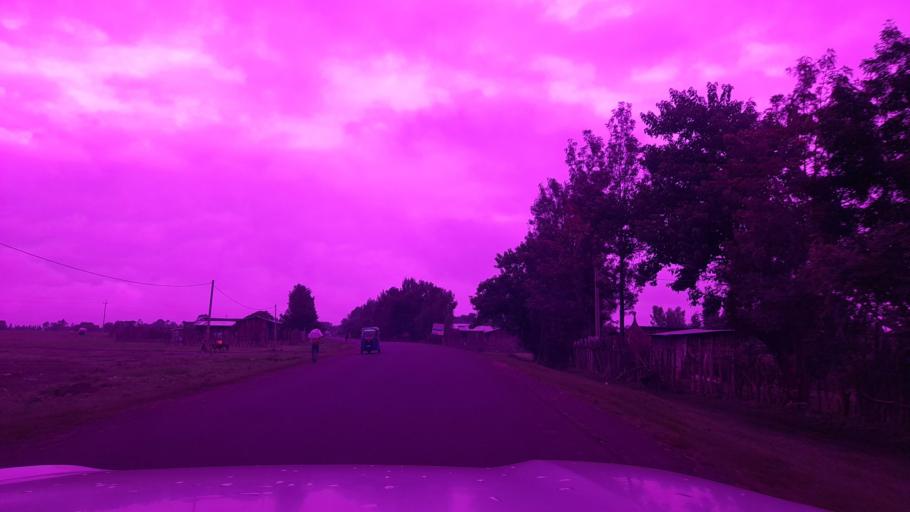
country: ET
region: Oromiya
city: Waliso
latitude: 8.2691
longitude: 37.6593
